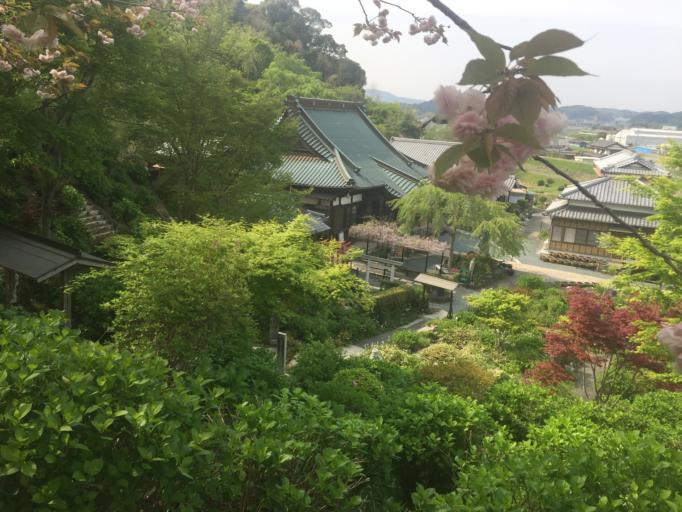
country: JP
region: Shizuoka
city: Kakegawa
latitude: 34.6874
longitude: 138.0527
